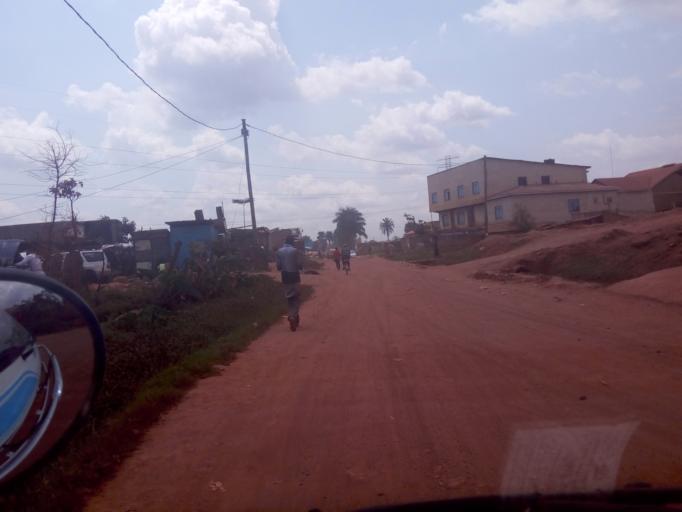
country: UG
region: Central Region
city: Kampala Central Division
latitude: 0.3460
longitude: 32.5576
